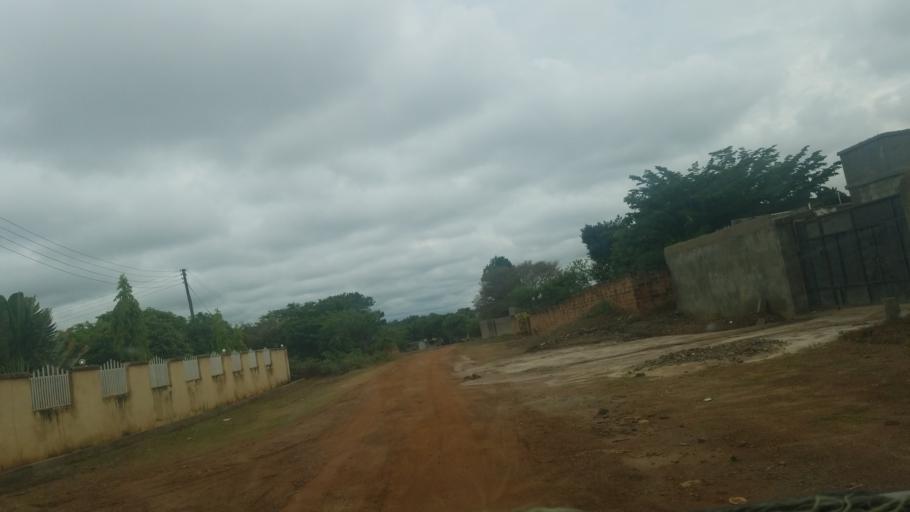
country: ZM
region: Luapula
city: Mansa
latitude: -11.1944
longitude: 28.9028
